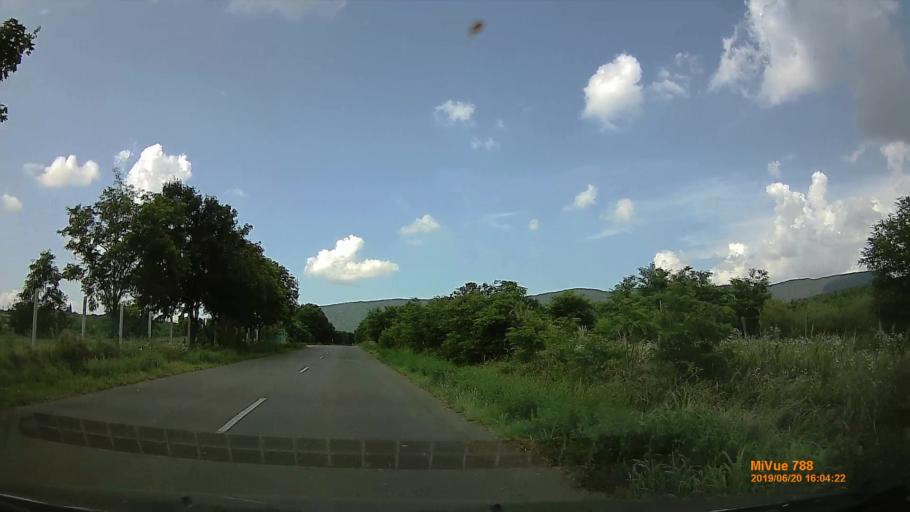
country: HU
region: Baranya
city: Pellerd
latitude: 46.0715
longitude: 18.1151
